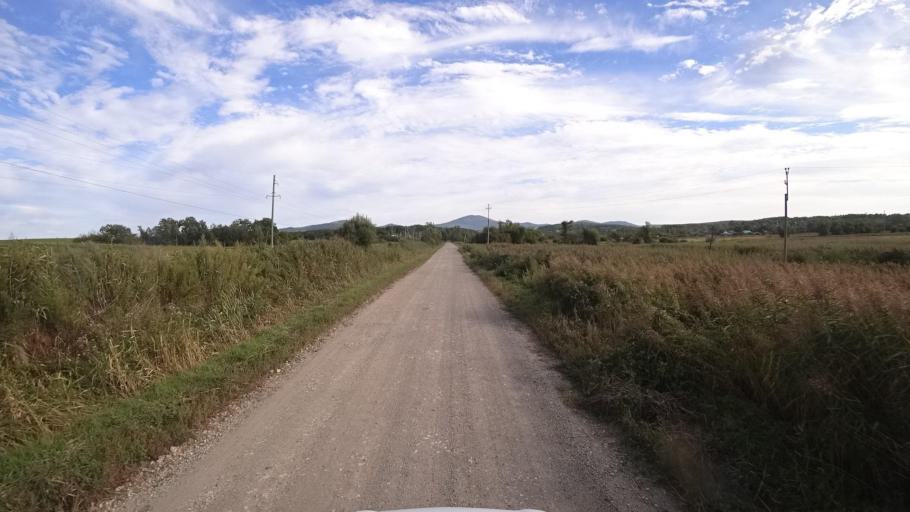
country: RU
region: Primorskiy
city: Dostoyevka
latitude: 44.3112
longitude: 133.4632
